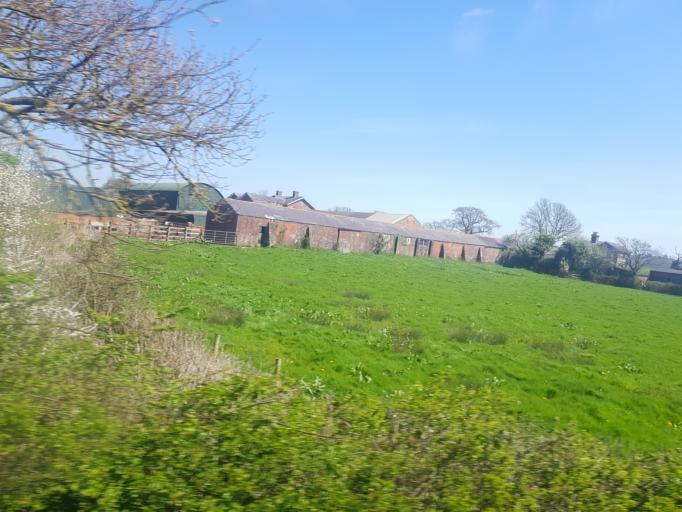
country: GB
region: England
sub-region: Isle of Wight
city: East Cowes
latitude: 50.7284
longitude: -1.2634
